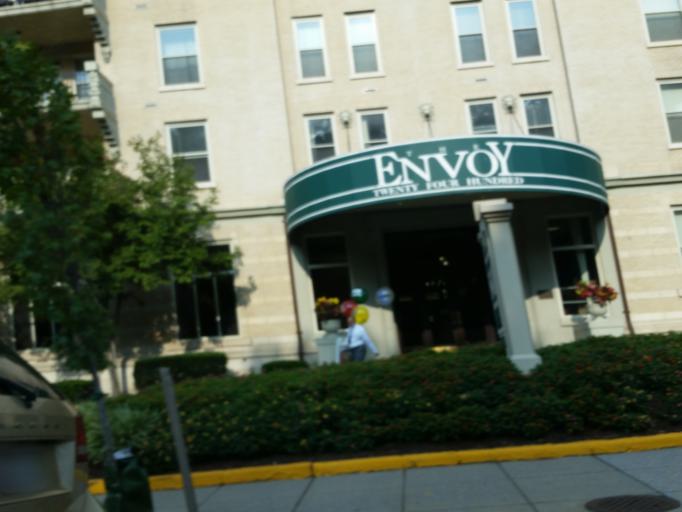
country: US
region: Washington, D.C.
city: Washington, D.C.
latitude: 38.9212
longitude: -77.0367
